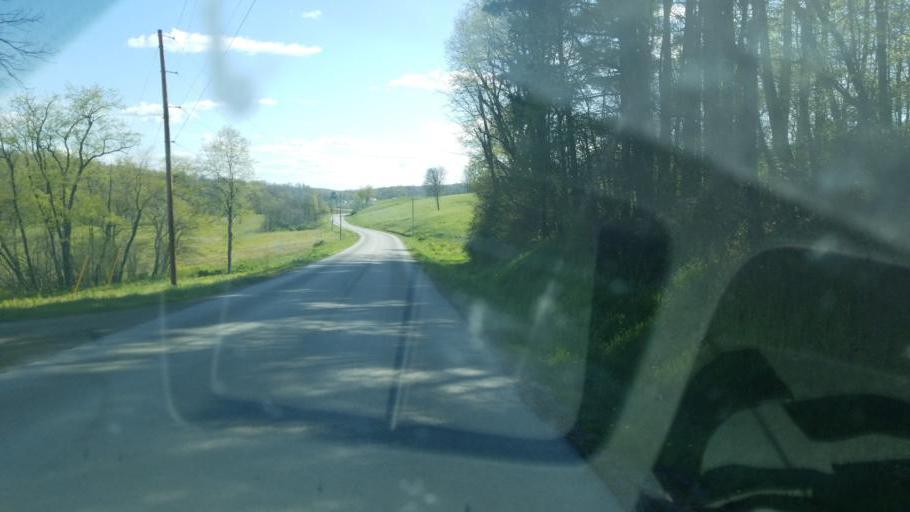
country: US
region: Ohio
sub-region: Coshocton County
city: Coshocton
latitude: 40.4071
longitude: -81.8346
